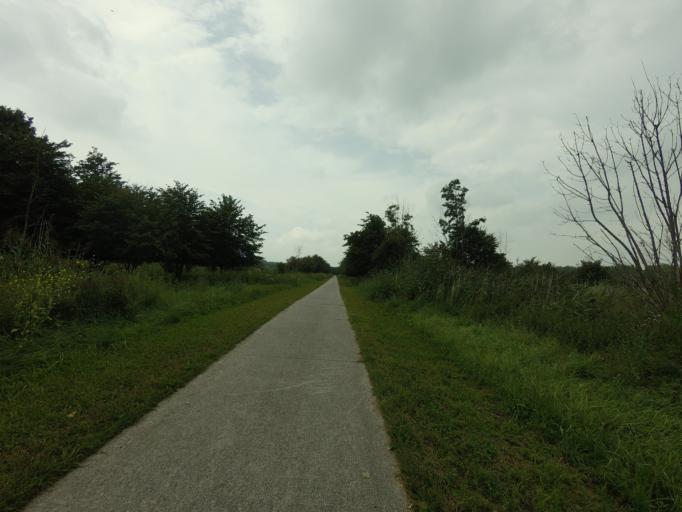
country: NL
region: Flevoland
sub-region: Gemeente Almere
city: Almere Stad
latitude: 52.4101
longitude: 5.3488
